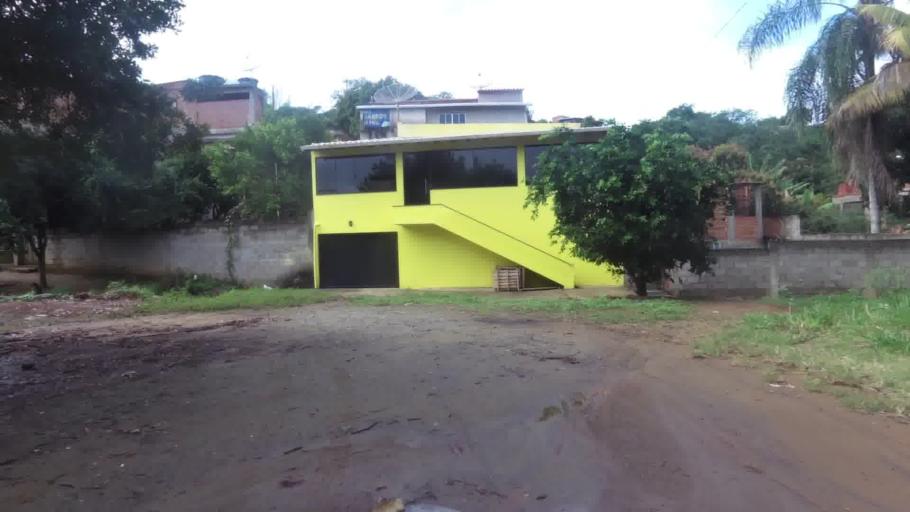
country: BR
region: Espirito Santo
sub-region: Piuma
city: Piuma
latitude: -20.8297
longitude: -40.7000
